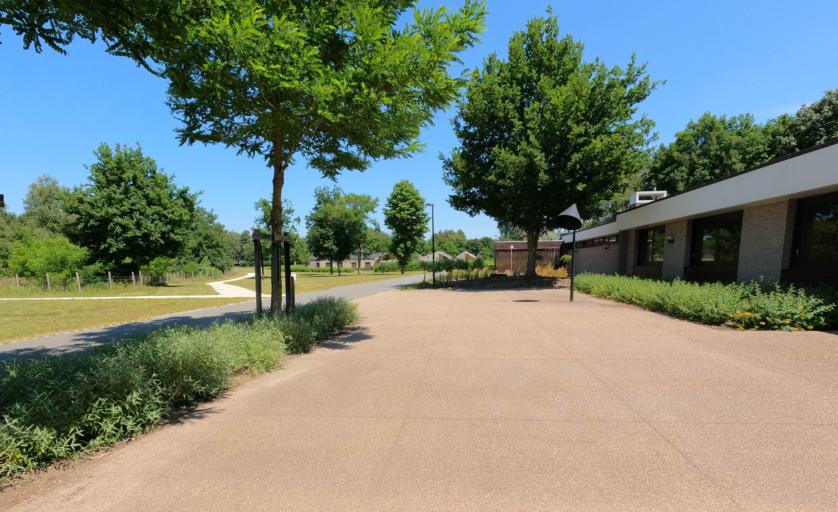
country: BE
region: Flanders
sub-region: Provincie Antwerpen
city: Beerse
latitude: 51.2925
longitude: 4.8592
